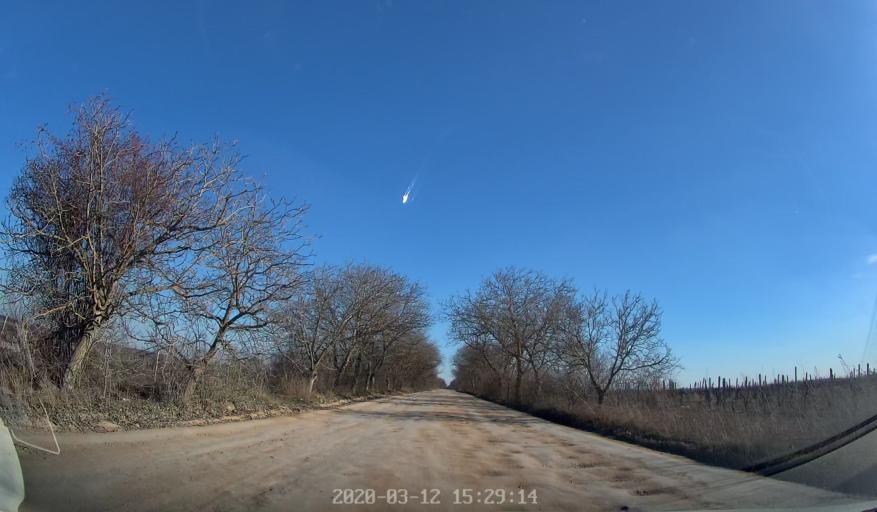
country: MD
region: Chisinau
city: Ciorescu
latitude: 47.1648
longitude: 28.9349
